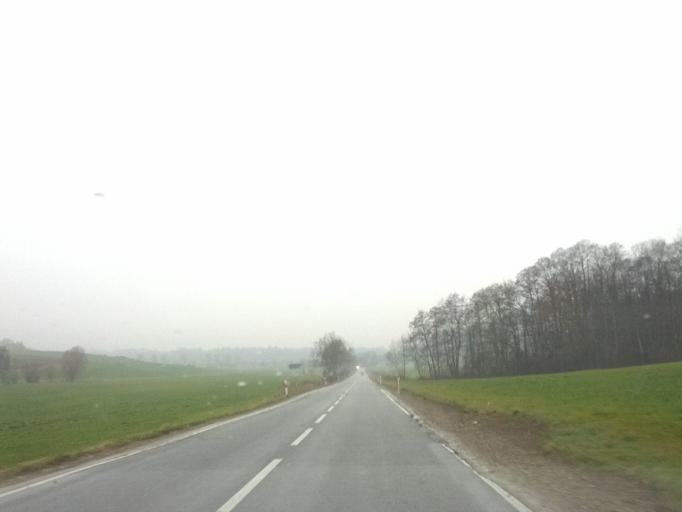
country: DE
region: Baden-Wuerttemberg
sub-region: Tuebingen Region
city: Ummendorf
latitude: 48.0734
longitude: 9.8417
